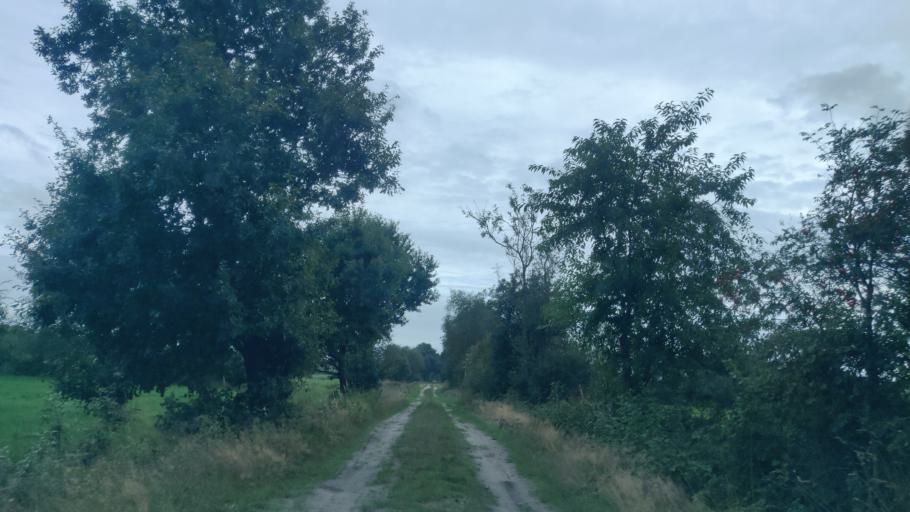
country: DE
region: Lower Saxony
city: Aurich
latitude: 53.5329
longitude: 7.4764
